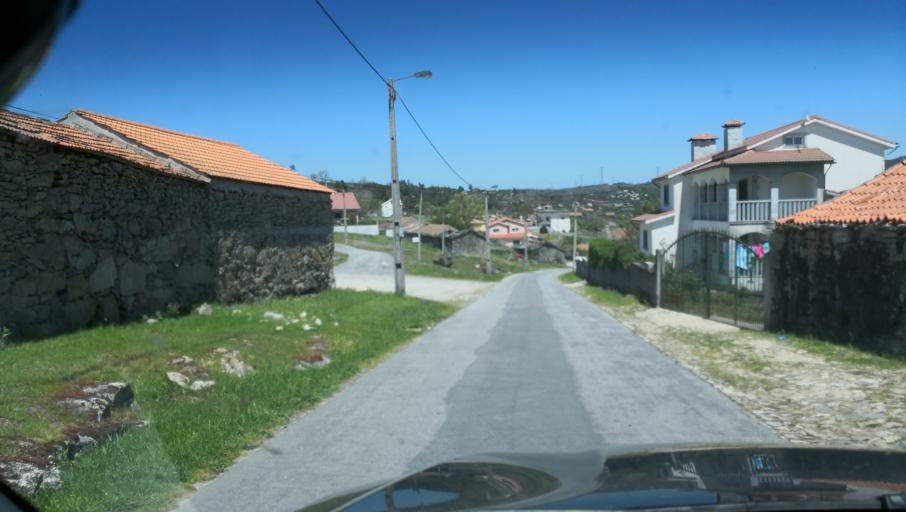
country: PT
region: Vila Real
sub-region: Sabrosa
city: Sabrosa
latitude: 41.2969
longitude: -7.6488
